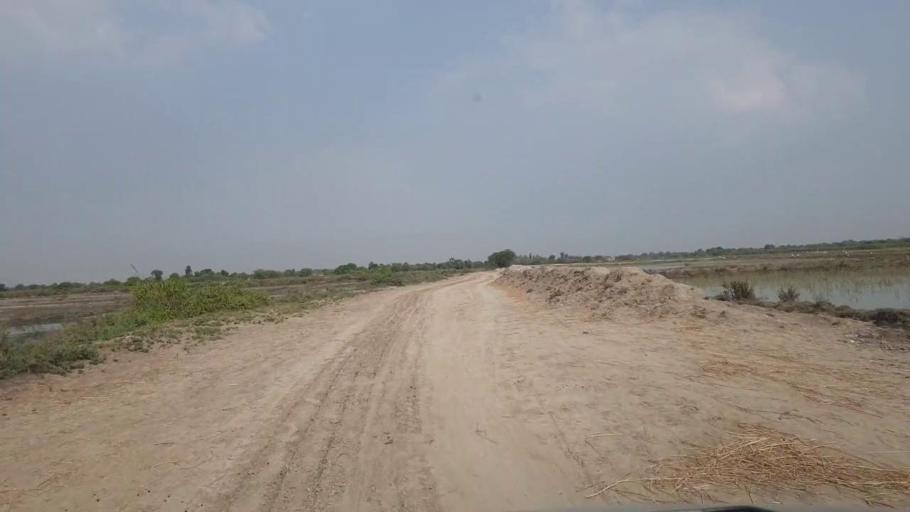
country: PK
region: Sindh
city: Matli
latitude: 24.9698
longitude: 68.6946
